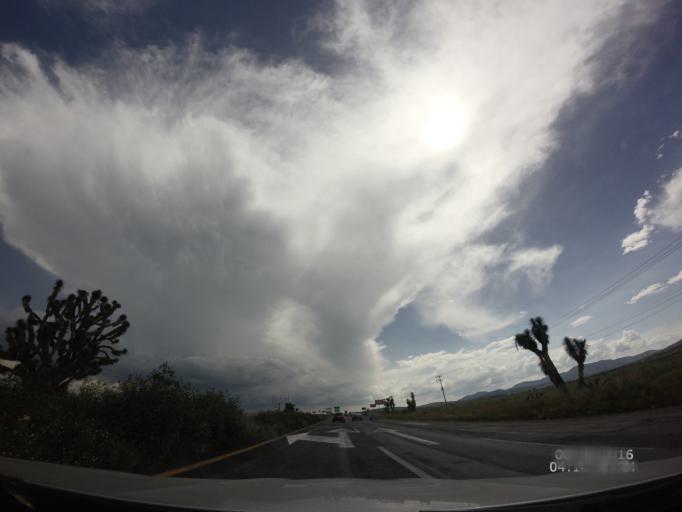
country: MX
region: Hidalgo
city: Acayuca
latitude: 20.0067
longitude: -98.8245
